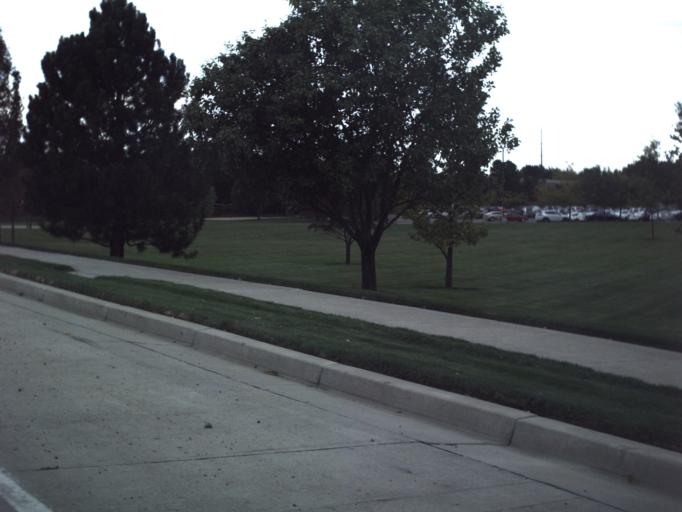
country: US
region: Utah
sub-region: Utah County
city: Provo
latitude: 40.2089
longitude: -111.6563
